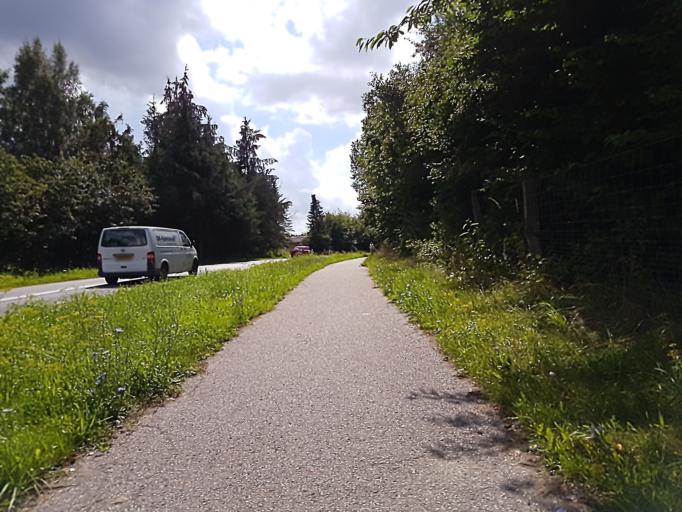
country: DK
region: Capital Region
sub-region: Ballerup Kommune
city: Malov
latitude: 55.7877
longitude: 12.3044
